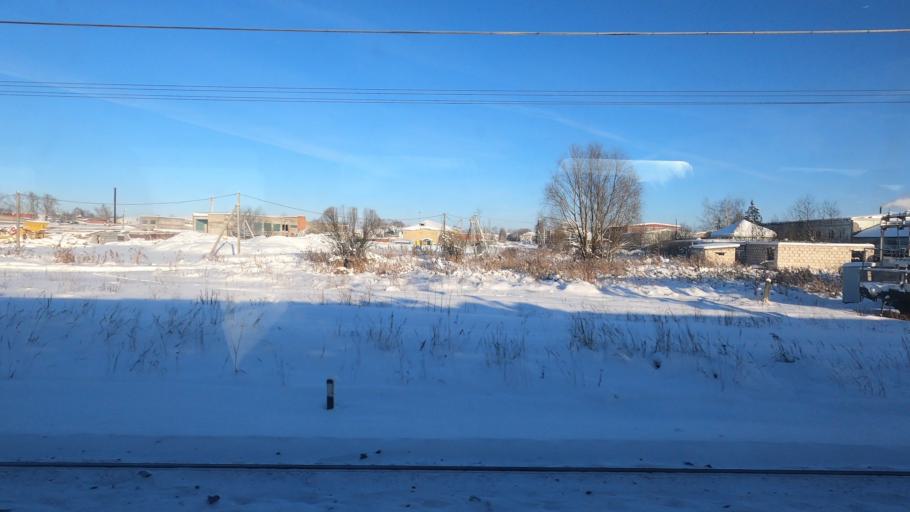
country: RU
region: Moskovskaya
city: Taldom
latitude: 56.7190
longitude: 37.5328
